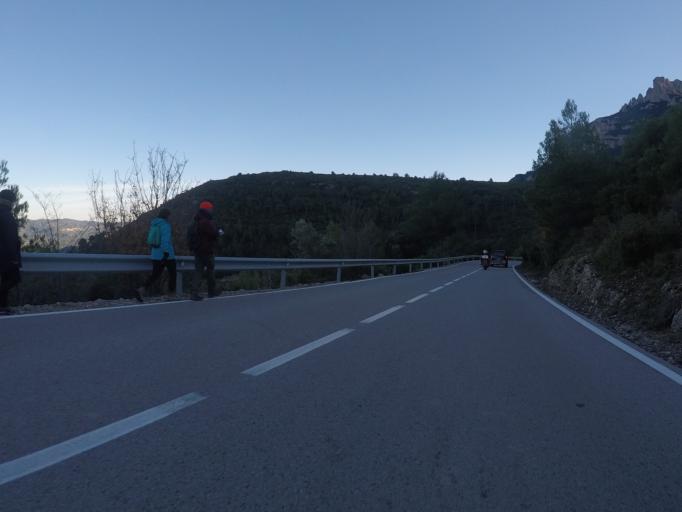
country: ES
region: Catalonia
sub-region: Provincia de Barcelona
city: Monistrol de Montserrat
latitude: 41.6160
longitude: 1.8311
